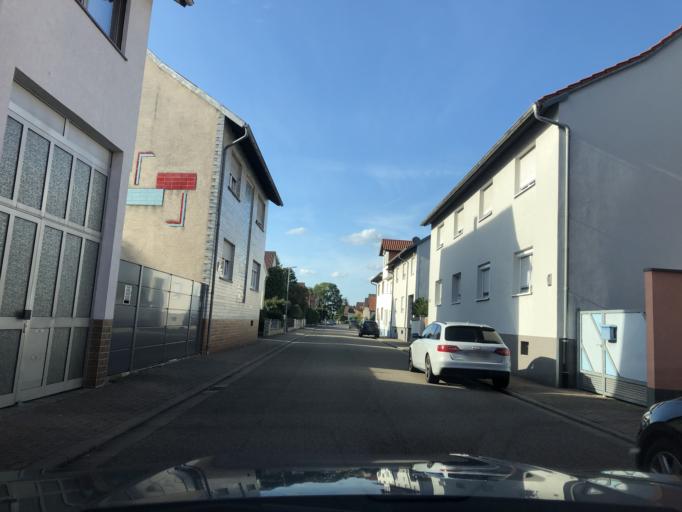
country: DE
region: Baden-Wuerttemberg
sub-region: Karlsruhe Region
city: Kronau
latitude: 49.2202
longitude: 8.6301
